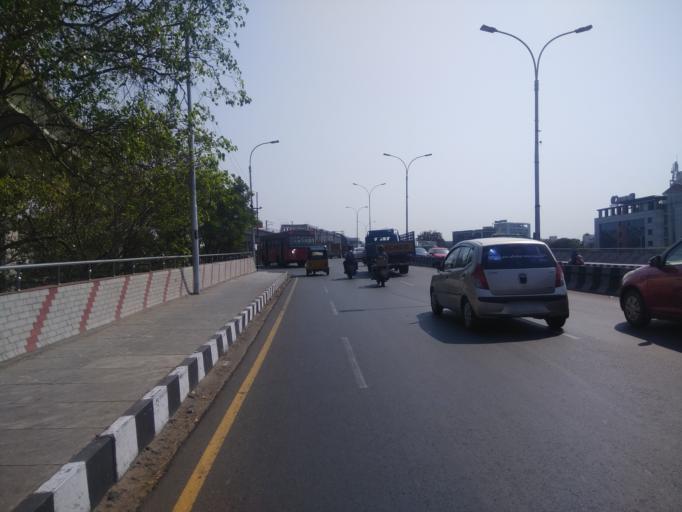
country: IN
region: Tamil Nadu
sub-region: Kancheepuram
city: Alandur
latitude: 13.0105
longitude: 80.2165
